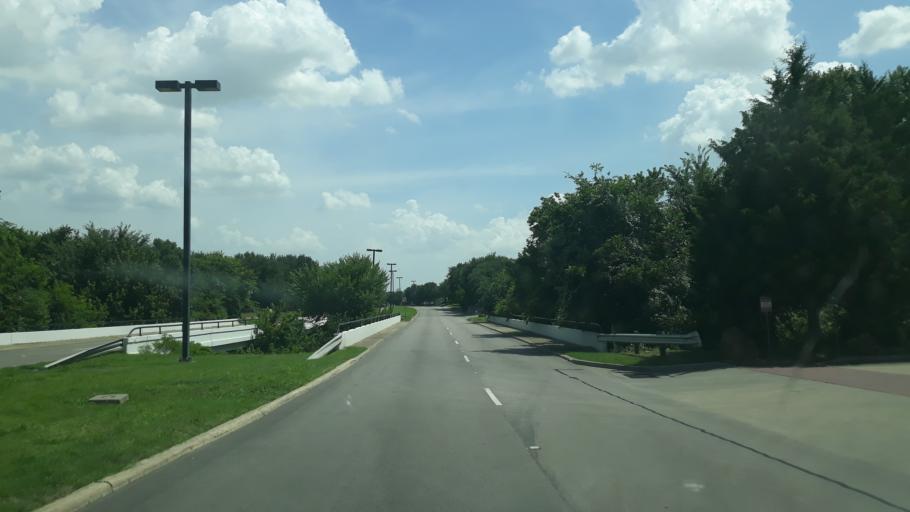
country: US
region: Texas
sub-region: Dallas County
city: Coppell
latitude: 32.9632
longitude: -97.0268
